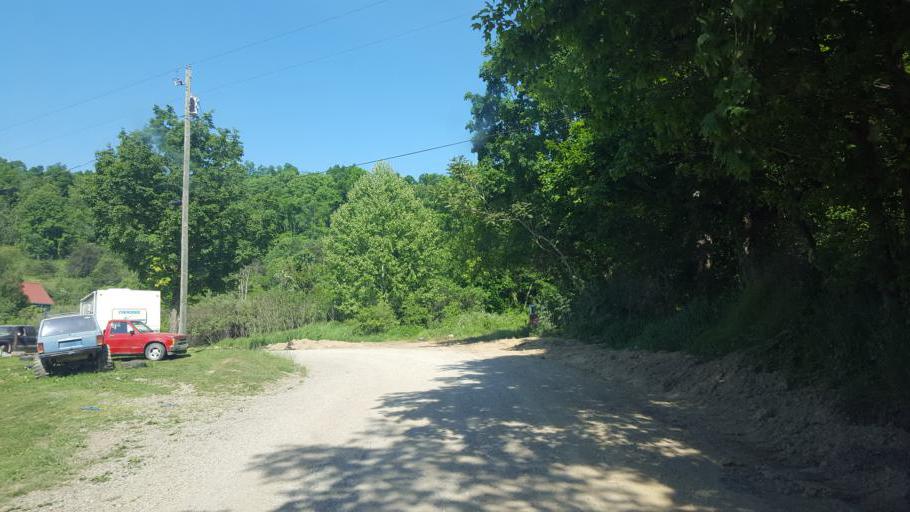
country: US
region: Ohio
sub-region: Jackson County
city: Wellston
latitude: 38.9958
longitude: -82.4166
